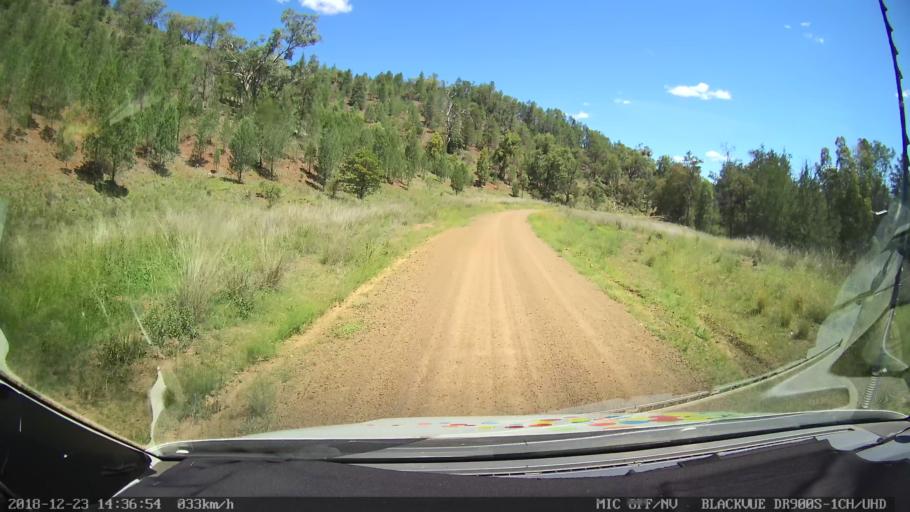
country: AU
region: New South Wales
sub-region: Tamworth Municipality
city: Manilla
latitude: -30.6126
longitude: 150.9085
